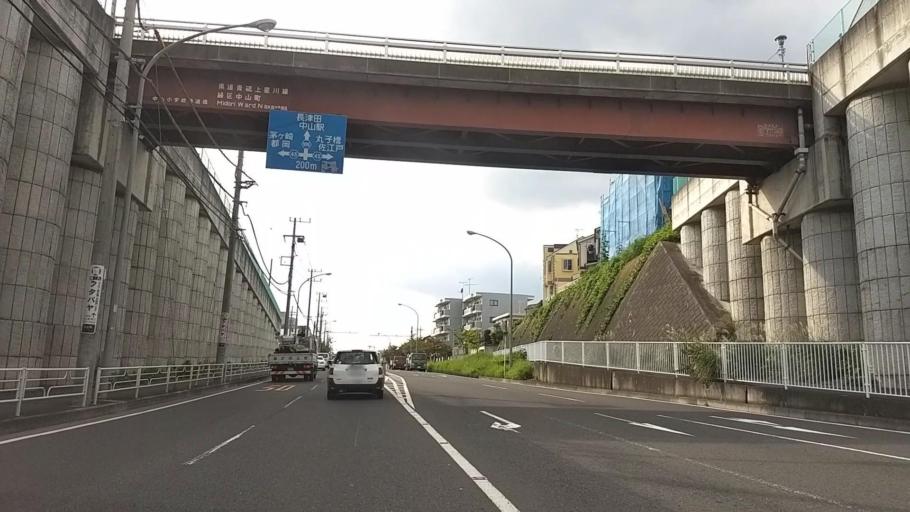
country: JP
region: Kanagawa
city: Minami-rinkan
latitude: 35.5096
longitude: 139.5485
